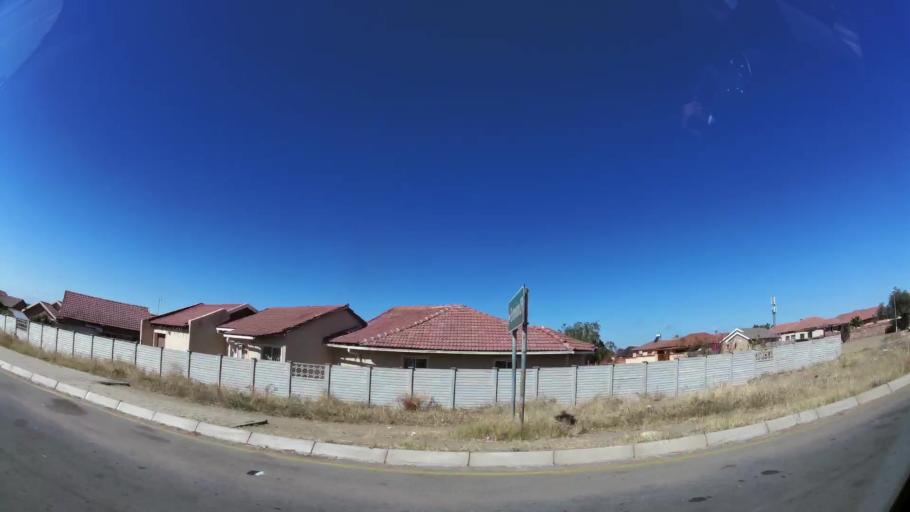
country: ZA
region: Limpopo
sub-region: Capricorn District Municipality
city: Polokwane
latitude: -23.8689
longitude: 29.4264
